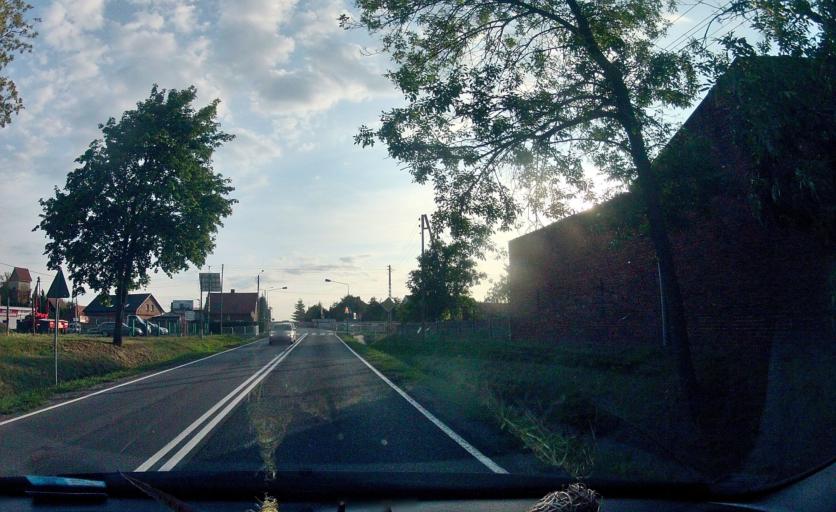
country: PL
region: Opole Voivodeship
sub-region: Powiat kluczborski
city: Kluczbork
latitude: 50.9466
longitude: 18.2249
